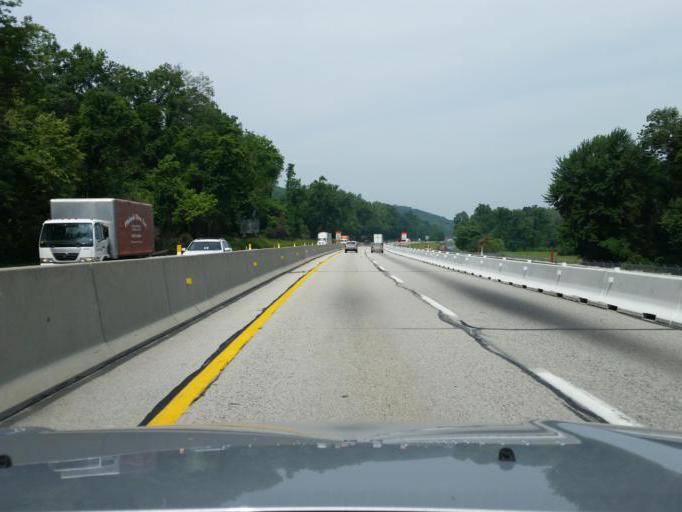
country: US
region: Pennsylvania
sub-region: Dauphin County
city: Bressler
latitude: 40.1974
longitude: -76.8291
